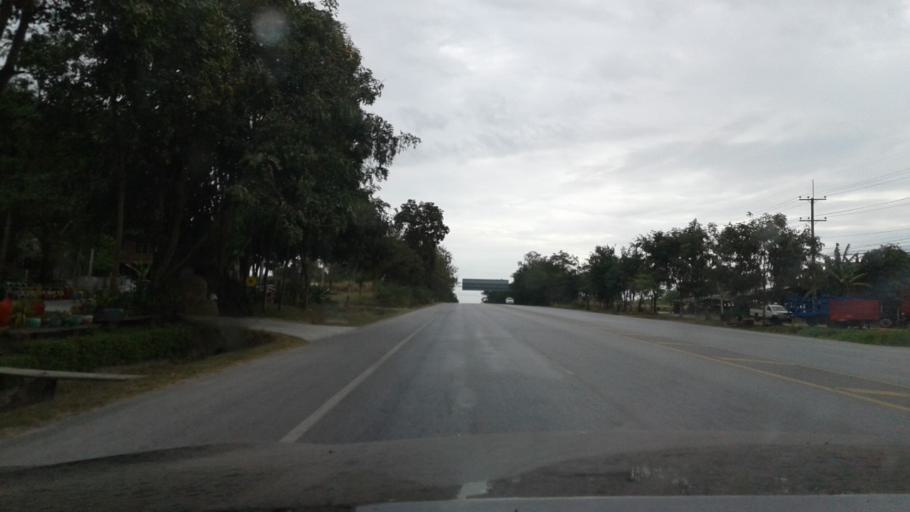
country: TH
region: Changwat Udon Thani
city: Nong Wua So
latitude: 17.2600
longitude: 102.5859
